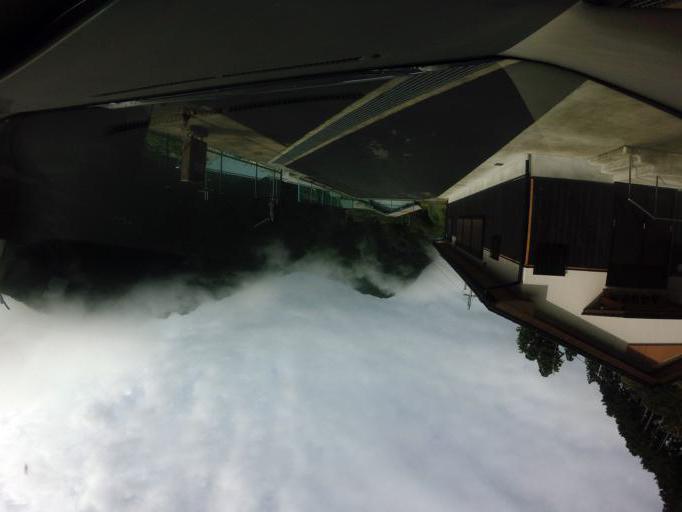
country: JP
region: Wakayama
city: Shingu
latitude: 33.9674
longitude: 135.8123
